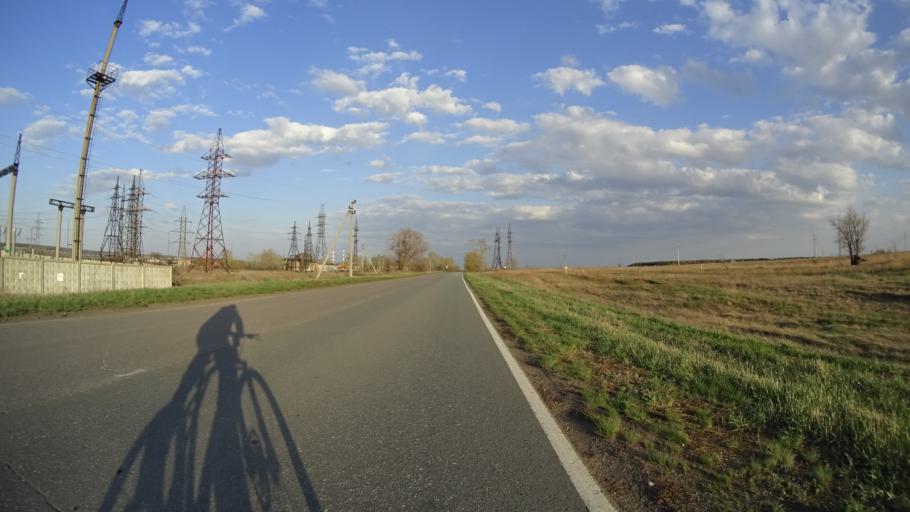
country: RU
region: Chelyabinsk
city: Troitsk
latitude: 54.0580
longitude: 61.5825
